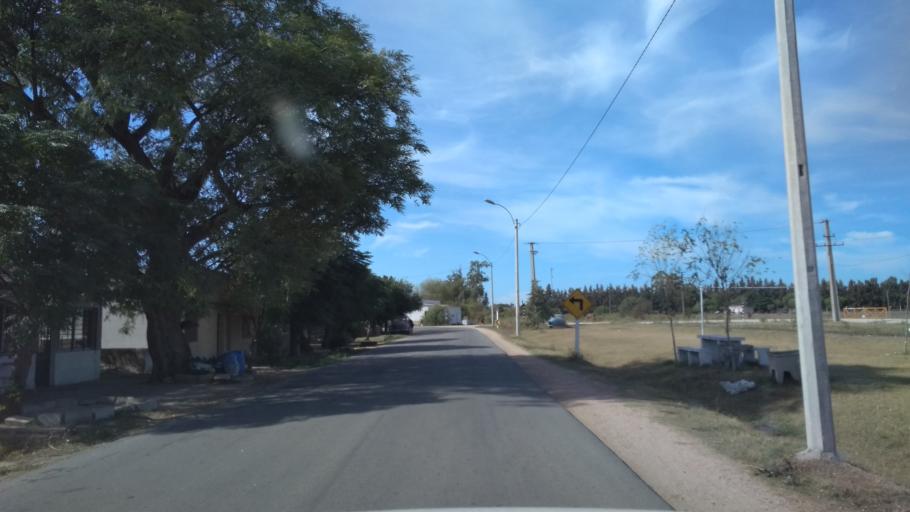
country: UY
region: Canelones
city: San Ramon
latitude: -34.2958
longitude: -55.9595
